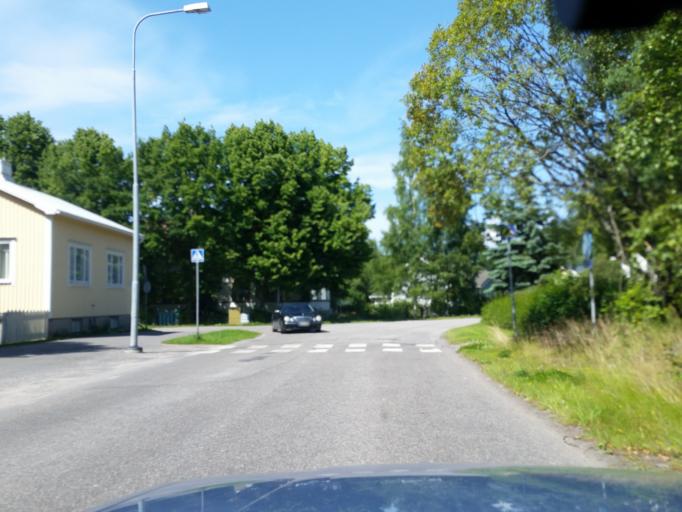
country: FI
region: Uusimaa
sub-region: Raaseporin
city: Hanko
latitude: 59.8366
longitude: 22.9435
